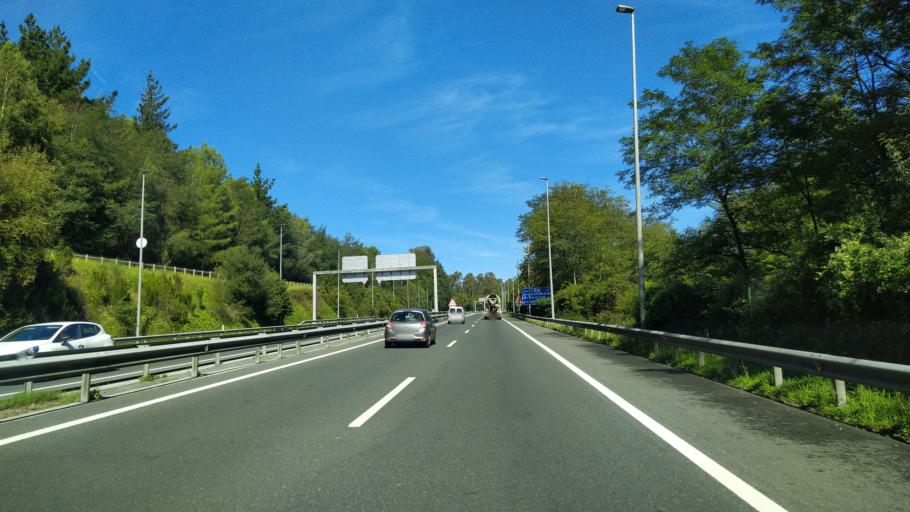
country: ES
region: Basque Country
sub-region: Bizkaia
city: Derio
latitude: 43.3105
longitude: -2.8796
